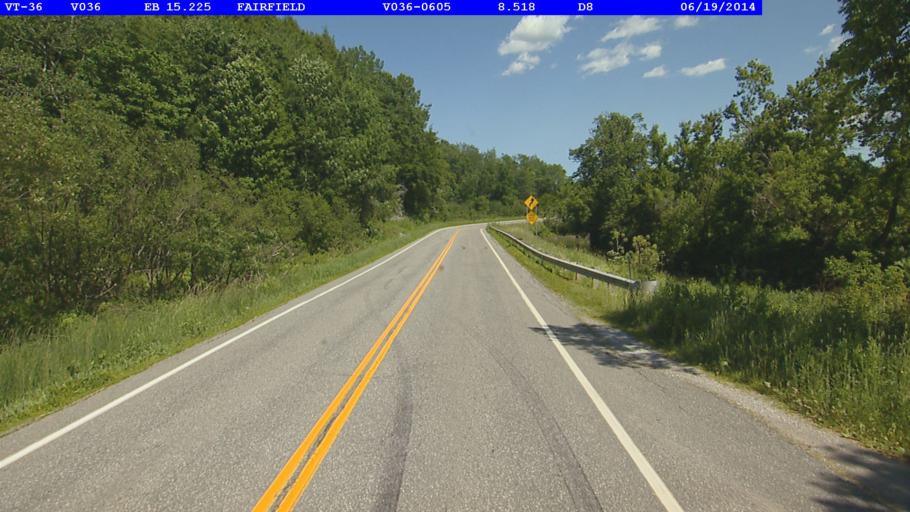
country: US
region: Vermont
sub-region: Franklin County
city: Enosburg Falls
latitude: 44.7934
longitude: -72.8723
